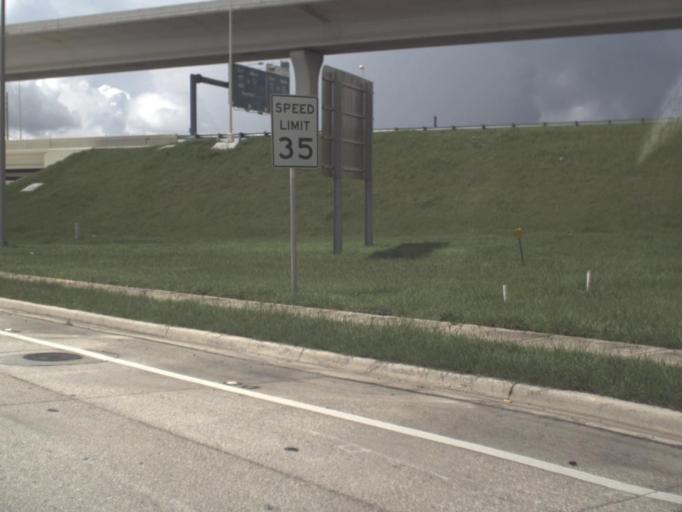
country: US
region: Florida
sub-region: Hillsborough County
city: Tampa
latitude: 27.9543
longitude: -82.4351
